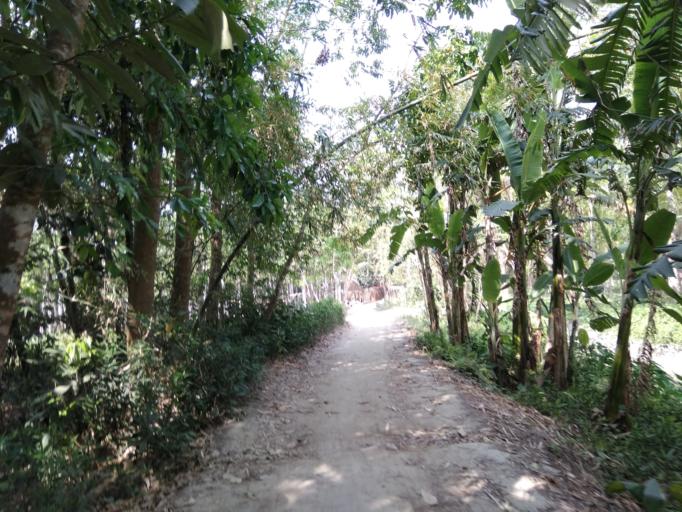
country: BD
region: Barisal
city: Gaurnadi
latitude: 22.9951
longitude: 90.3748
